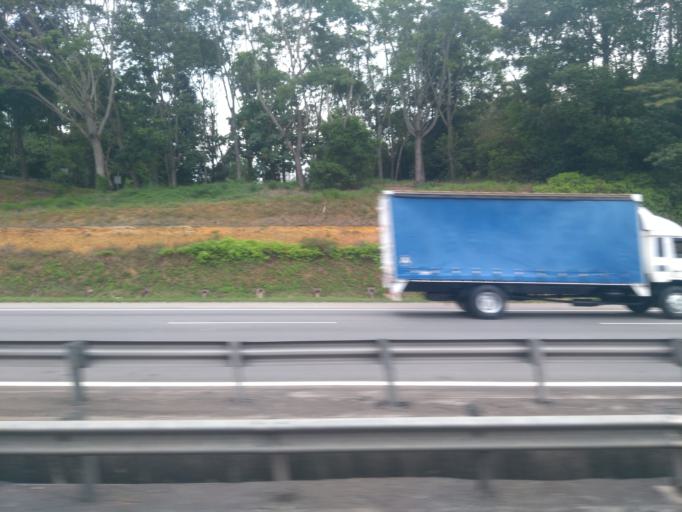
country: MY
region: Negeri Sembilan
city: Kampung Baharu Nilai
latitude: 2.8506
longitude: 101.7877
